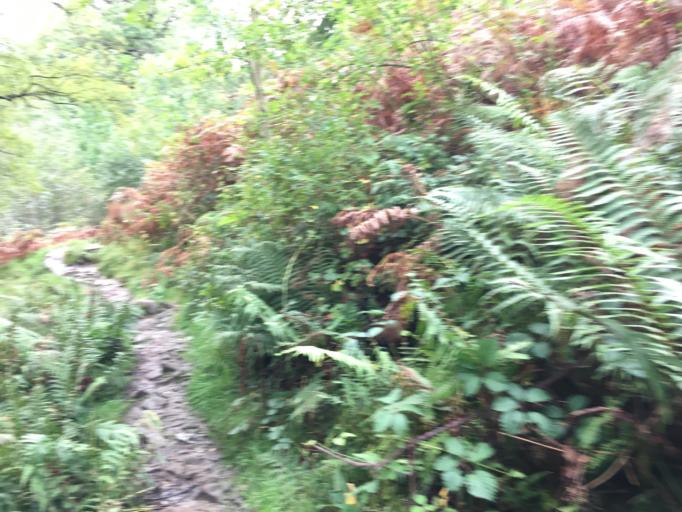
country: GB
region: England
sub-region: North Yorkshire
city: Sleights
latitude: 54.4091
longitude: -0.7331
